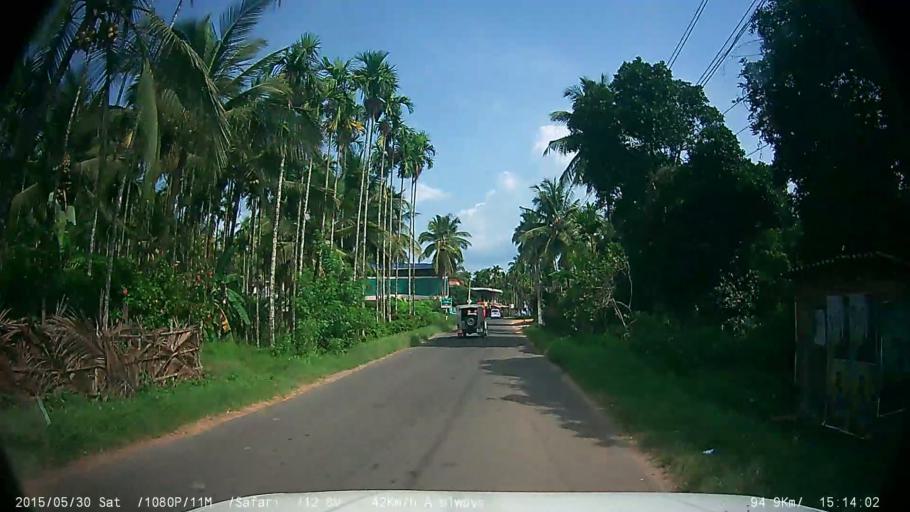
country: IN
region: Kerala
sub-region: Wayanad
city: Panamaram
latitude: 11.7882
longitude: 76.0453
